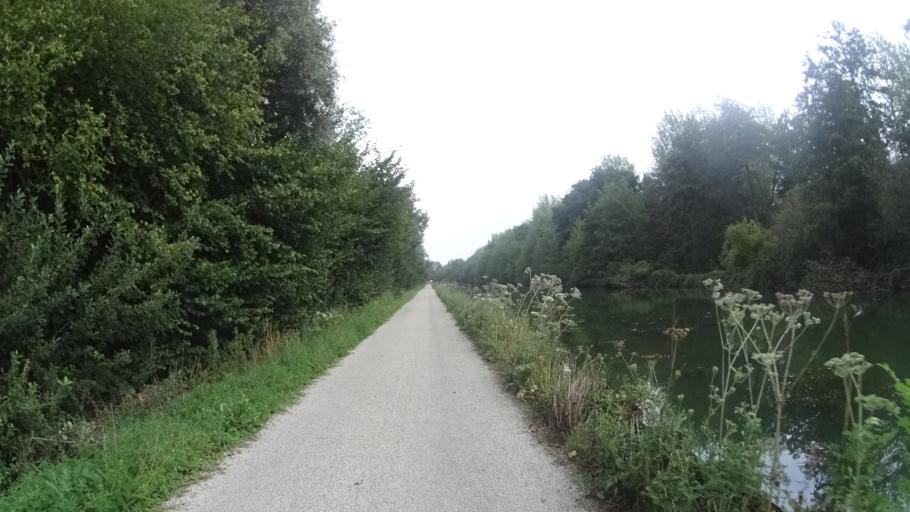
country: FR
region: Picardie
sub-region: Departement de l'Aisne
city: Ribemont
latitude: 49.7829
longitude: 3.4126
